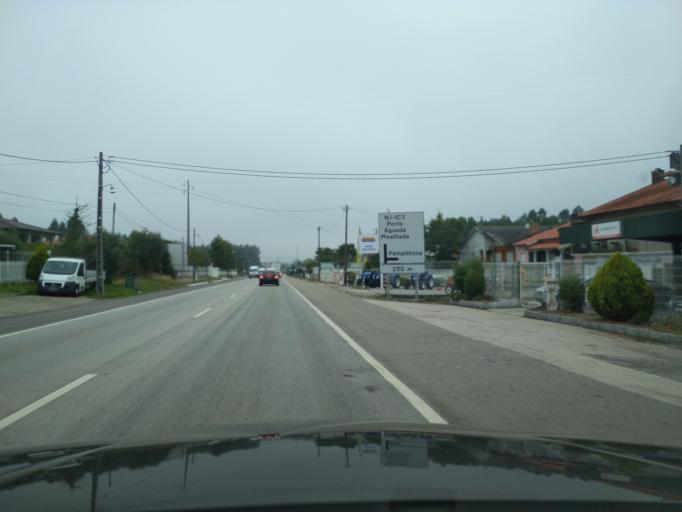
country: PT
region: Aveiro
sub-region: Mealhada
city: Pampilhosa do Botao
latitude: 40.3093
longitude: -8.4494
